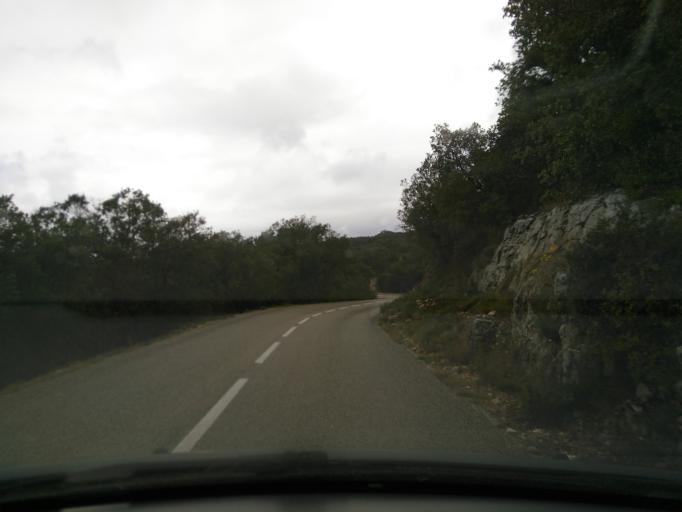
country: FR
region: Languedoc-Roussillon
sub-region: Departement du Gard
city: Barjac
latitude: 44.3201
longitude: 4.4246
